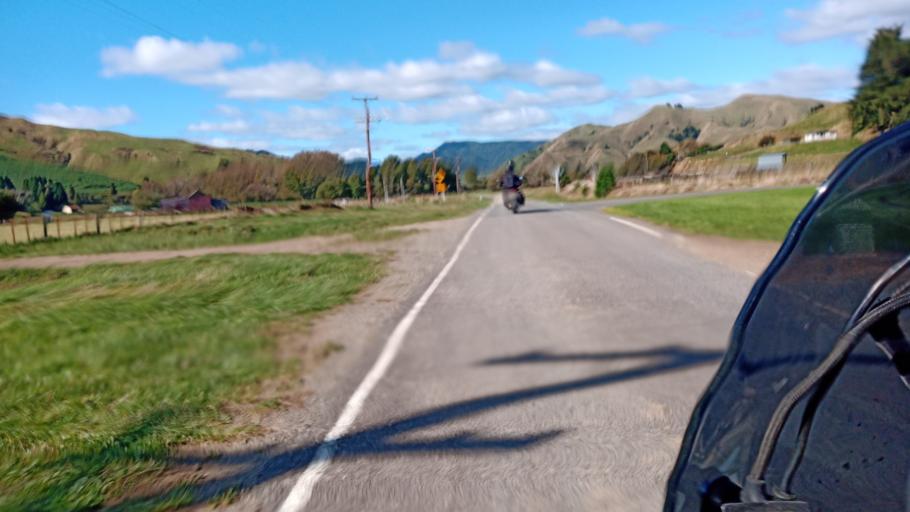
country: NZ
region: Bay of Plenty
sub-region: Opotiki District
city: Opotiki
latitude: -38.2556
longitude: 177.5497
